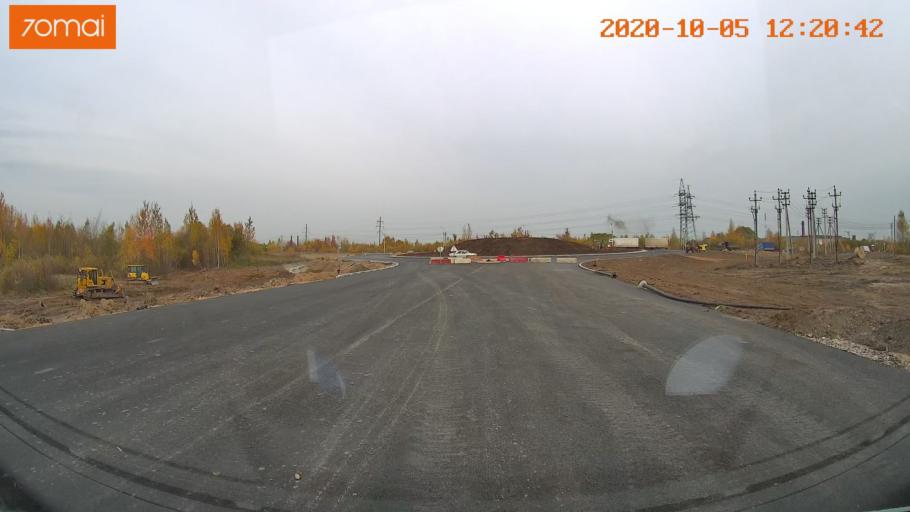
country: RU
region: Ivanovo
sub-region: Gorod Ivanovo
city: Ivanovo
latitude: 56.9658
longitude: 40.9315
